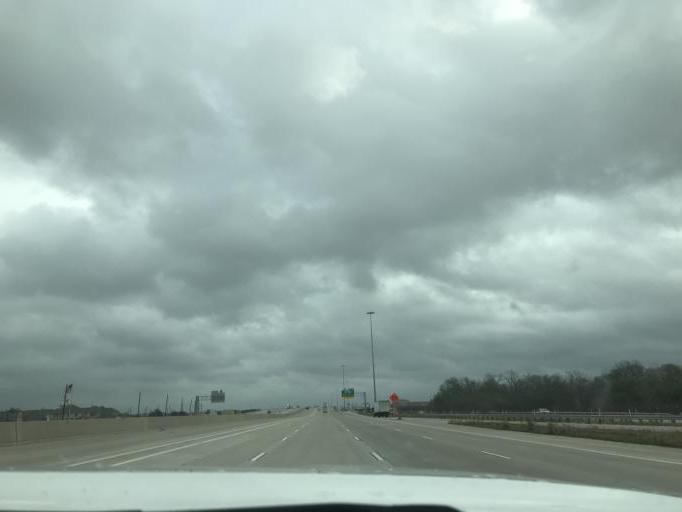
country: US
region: Texas
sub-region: Fort Bend County
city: Richmond
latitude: 29.5545
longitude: -95.7233
